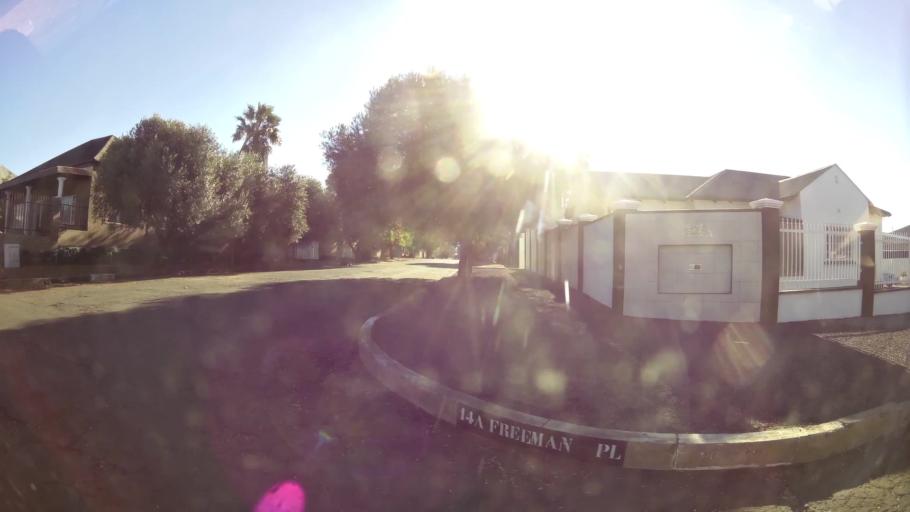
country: ZA
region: Northern Cape
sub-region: Frances Baard District Municipality
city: Kimberley
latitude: -28.7540
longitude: 24.7863
